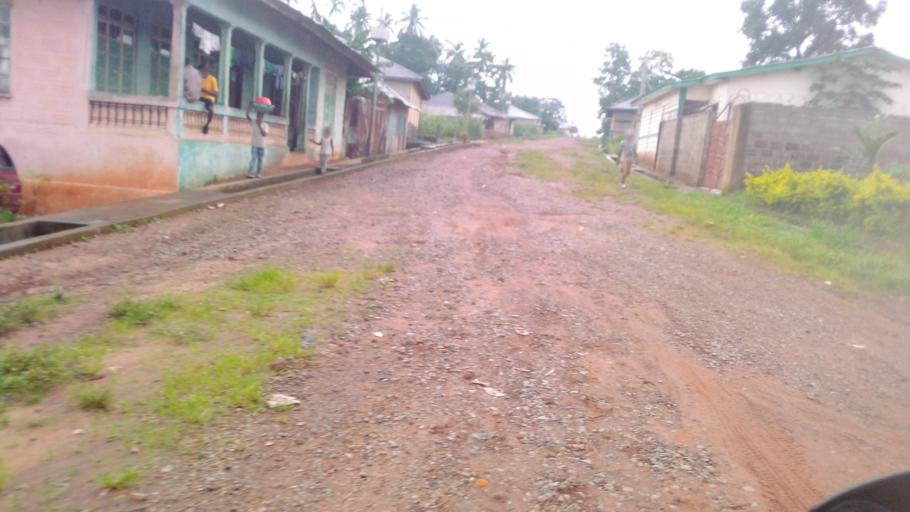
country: SL
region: Northern Province
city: Lunsar
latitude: 8.6814
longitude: -12.5298
